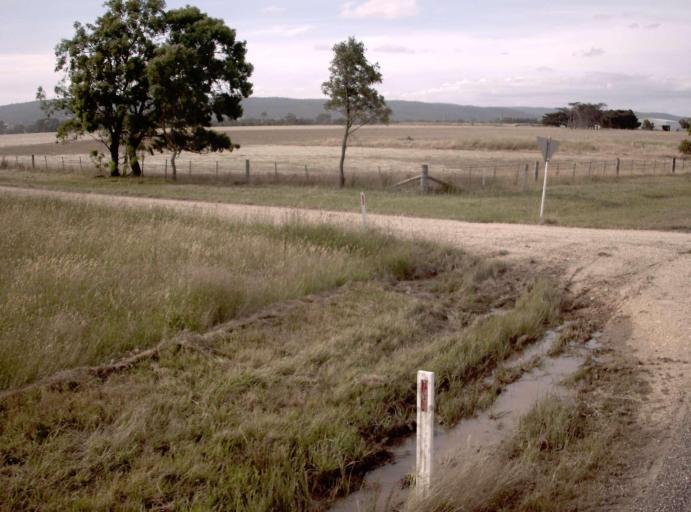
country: AU
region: Victoria
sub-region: Wellington
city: Heyfield
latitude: -38.0543
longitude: 146.6630
